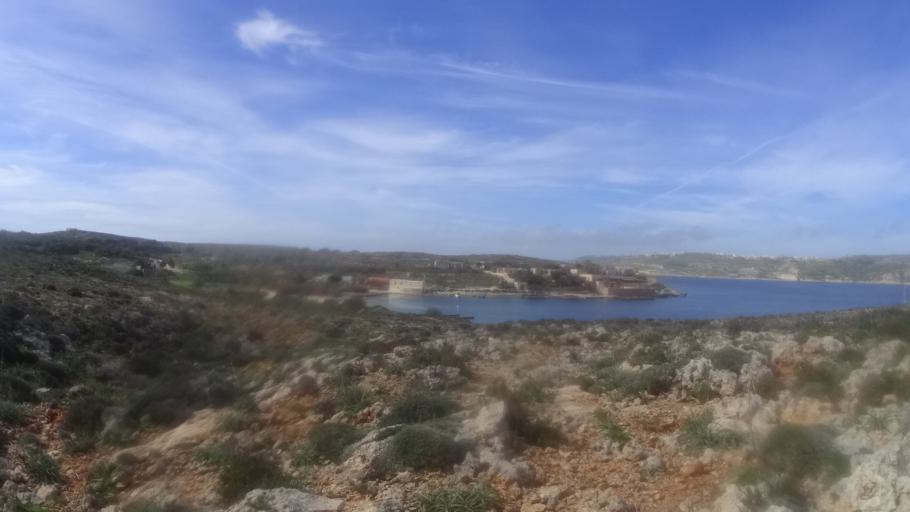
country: MT
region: Il-Qala
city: Qala
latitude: 36.0163
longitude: 14.3395
